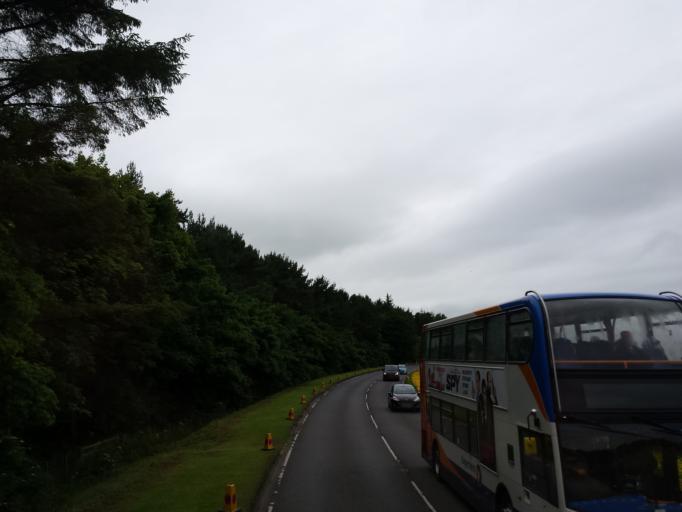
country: GB
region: Scotland
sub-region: Fife
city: Saint Andrews
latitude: 56.3426
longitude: -2.8153
